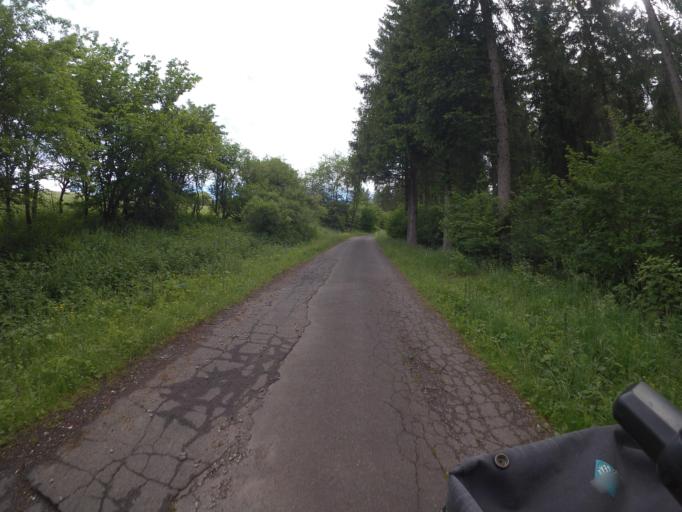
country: DE
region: Rheinland-Pfalz
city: Scheid
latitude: 50.4032
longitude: 6.3887
